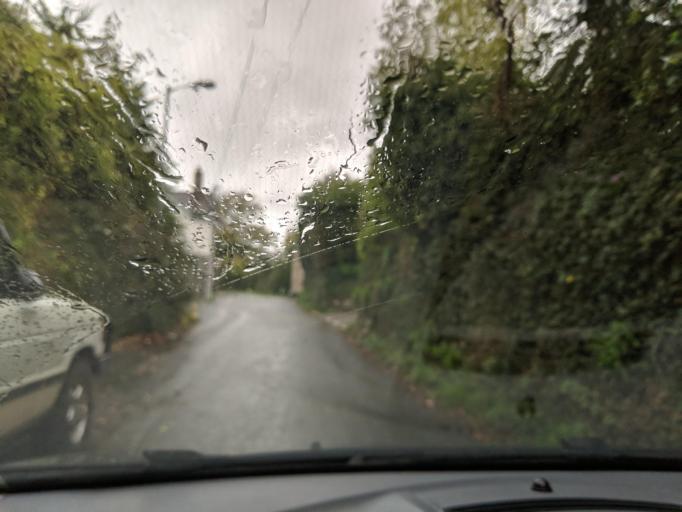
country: GB
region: England
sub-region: Cornwall
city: Wadebridge
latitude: 50.5146
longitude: -4.8213
